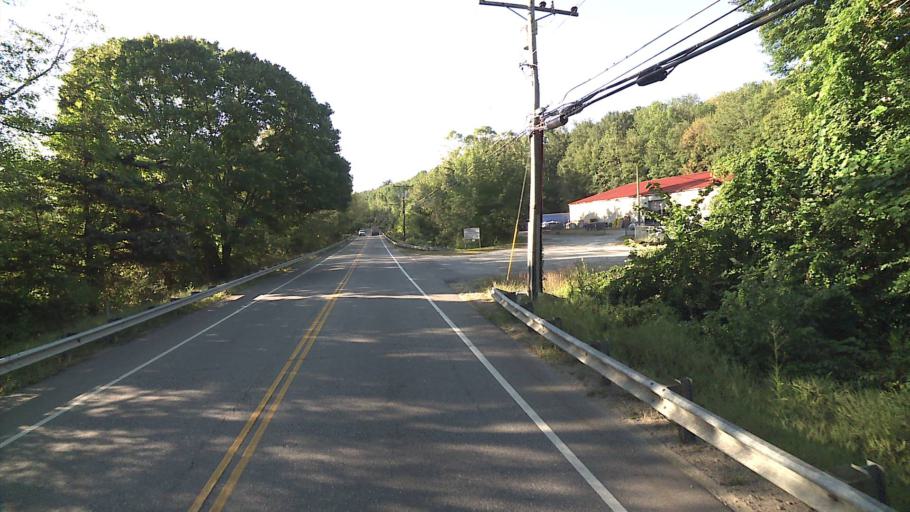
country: US
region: Connecticut
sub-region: Windham County
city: South Windham
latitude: 41.6764
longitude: -72.1676
